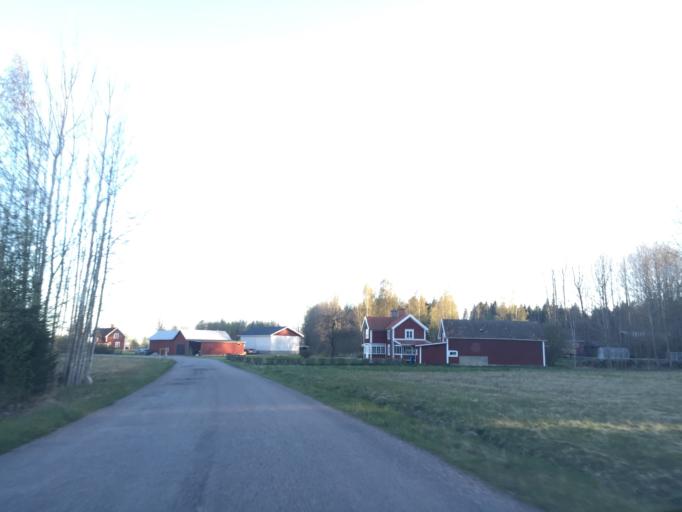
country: SE
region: OErebro
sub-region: Orebro Kommun
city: Odensbacken
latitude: 59.2197
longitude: 15.5603
